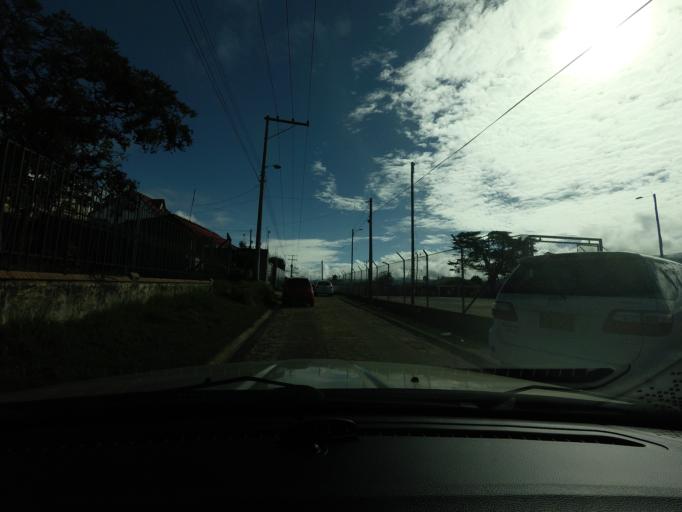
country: CO
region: Cundinamarca
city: La Calera
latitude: 4.7619
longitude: -74.0159
